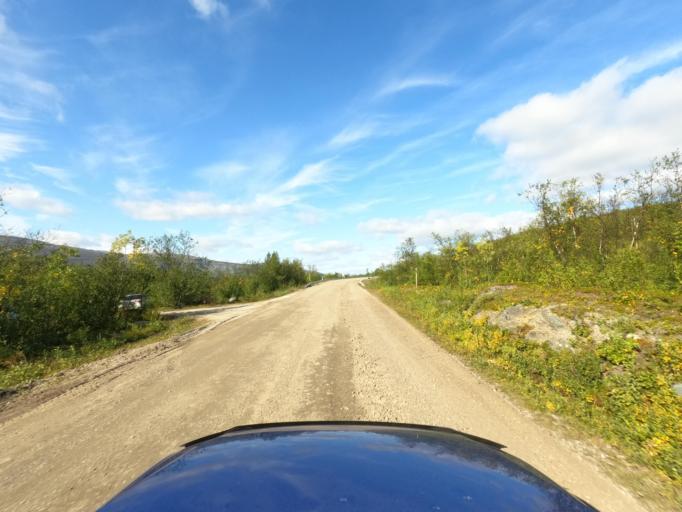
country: NO
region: Finnmark Fylke
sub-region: Porsanger
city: Lakselv
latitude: 69.8793
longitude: 25.0239
